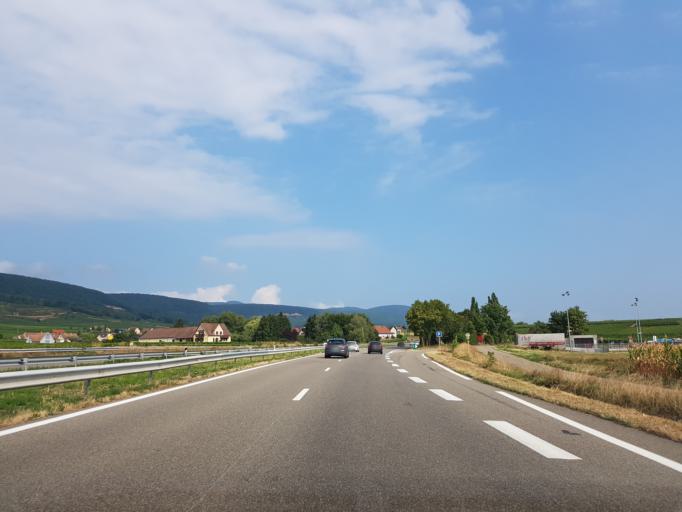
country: FR
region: Alsace
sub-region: Departement du Haut-Rhin
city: Pfaffenheim
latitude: 47.9762
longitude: 7.2956
